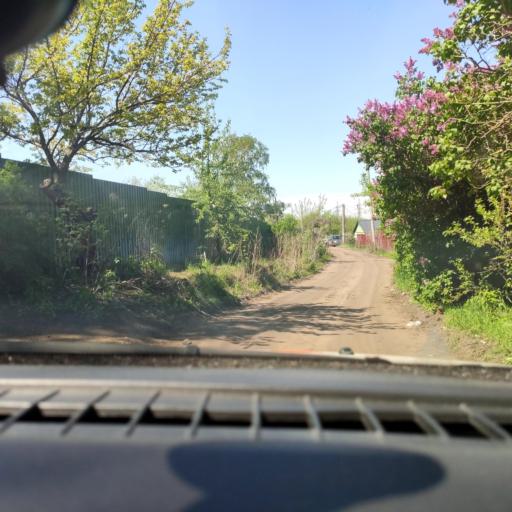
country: RU
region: Voronezj
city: Maslovka
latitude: 51.6116
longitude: 39.2779
